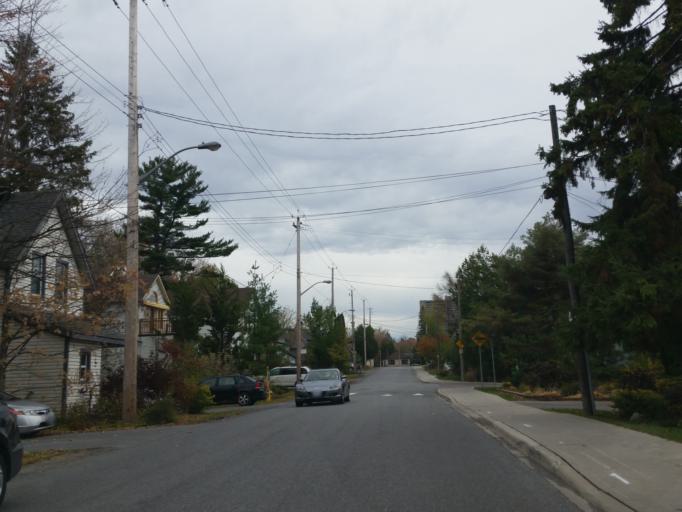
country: CA
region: Ontario
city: Bells Corners
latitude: 45.3672
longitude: -75.7978
